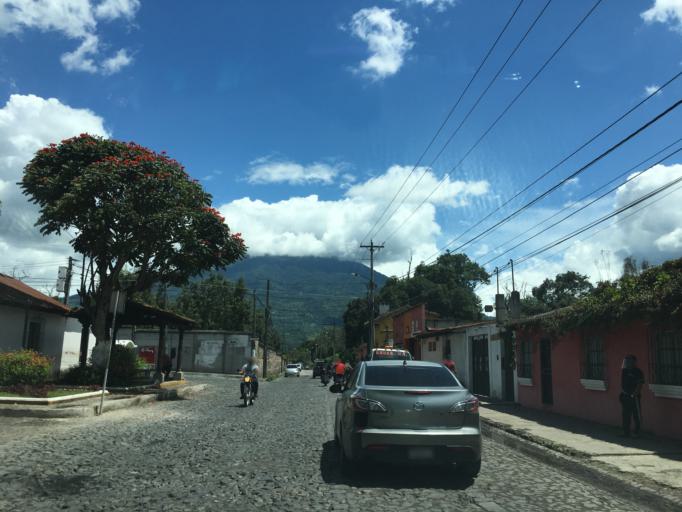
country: GT
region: Sacatepequez
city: Antigua Guatemala
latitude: 14.5491
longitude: -90.7285
